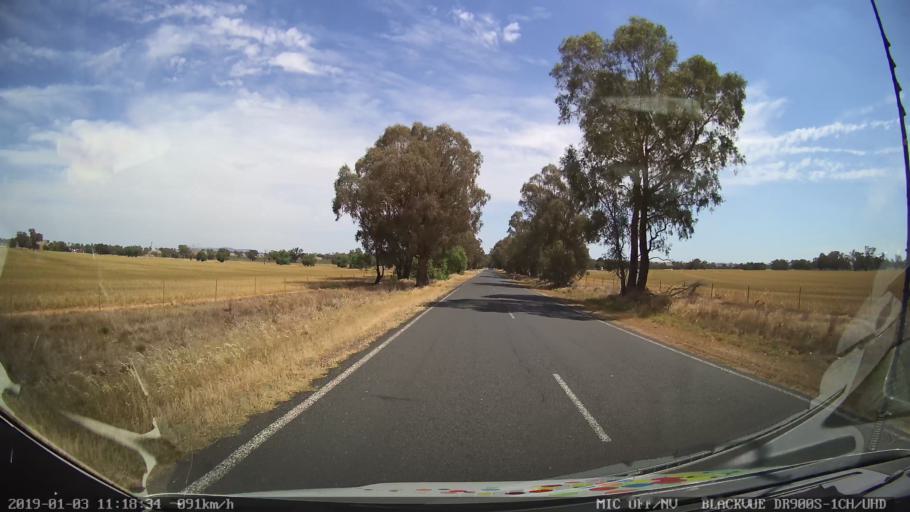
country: AU
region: New South Wales
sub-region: Young
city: Young
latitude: -34.1243
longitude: 148.2619
